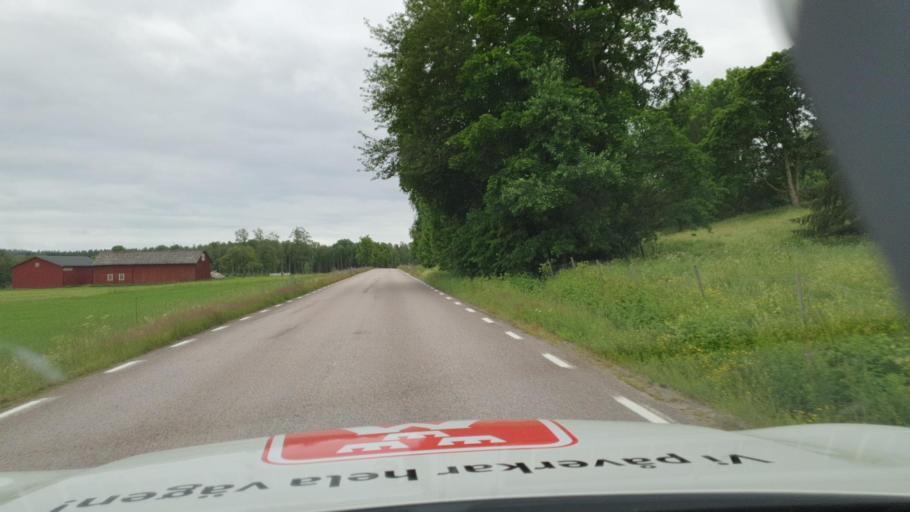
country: SE
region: Vaermland
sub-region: Sunne Kommun
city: Sunne
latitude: 59.7216
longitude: 13.2244
